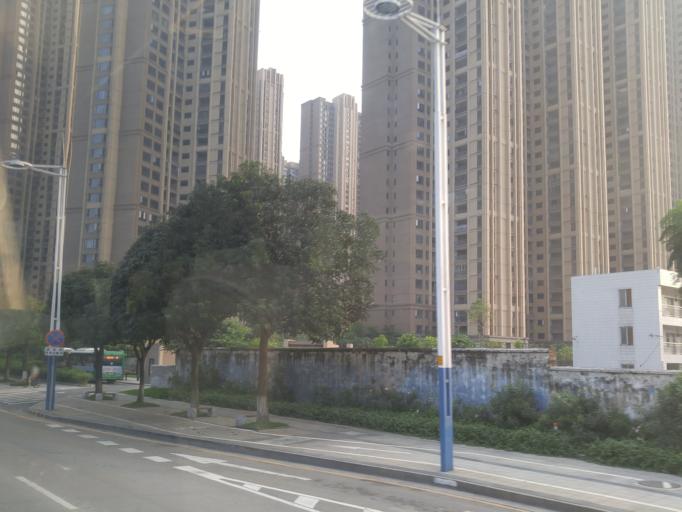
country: CN
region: Guangdong
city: Foshan
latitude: 23.0687
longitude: 113.1405
